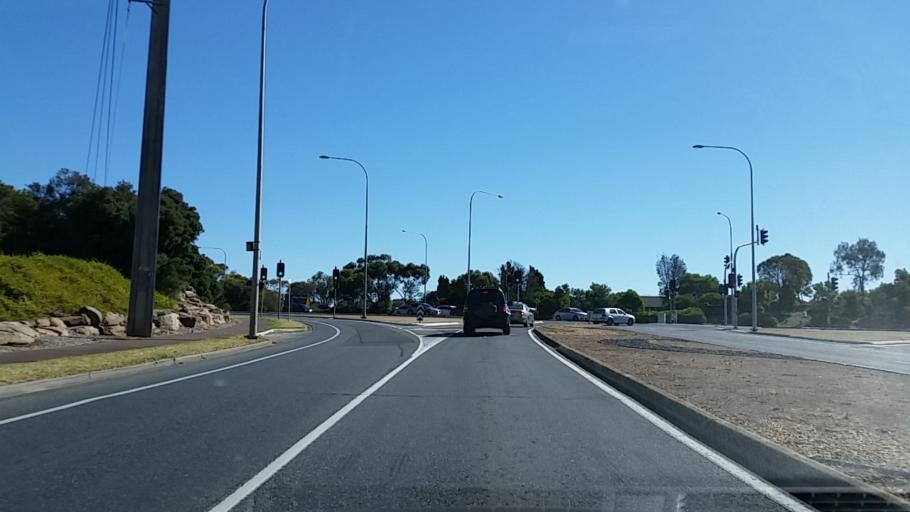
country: AU
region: South Australia
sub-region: Tea Tree Gully
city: Modbury
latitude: -34.8111
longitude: 138.6755
